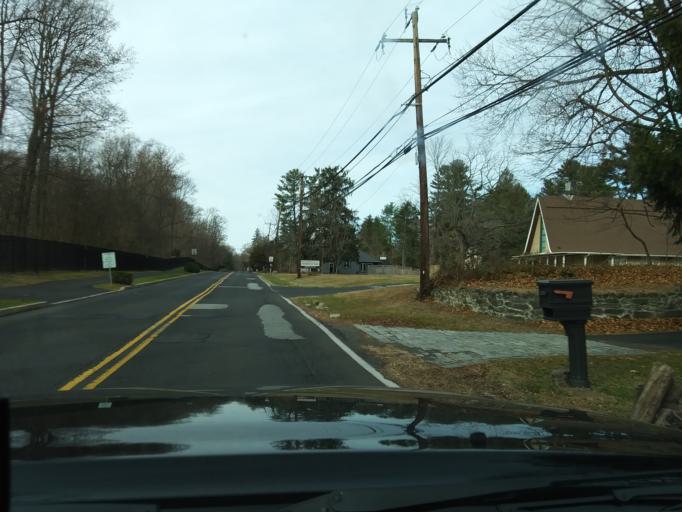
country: US
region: Pennsylvania
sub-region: Montgomery County
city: Jenkintown
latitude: 40.0909
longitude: -75.1073
